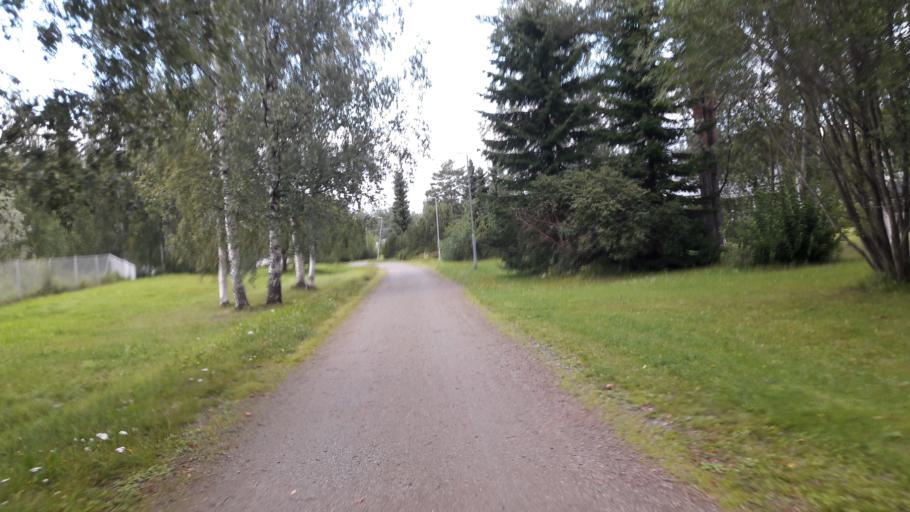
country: FI
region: North Karelia
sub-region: Joensuu
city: Joensuu
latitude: 62.5945
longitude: 29.7956
